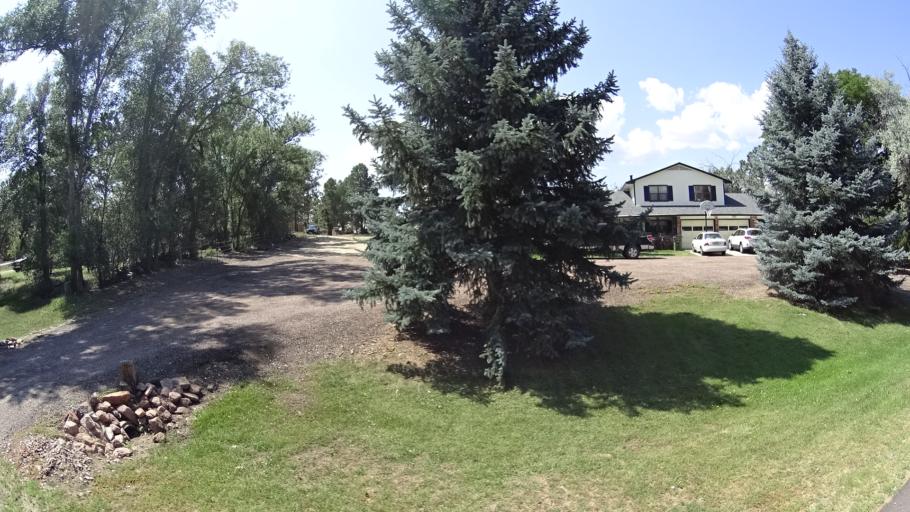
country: US
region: Colorado
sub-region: El Paso County
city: Air Force Academy
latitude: 38.9383
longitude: -104.7954
